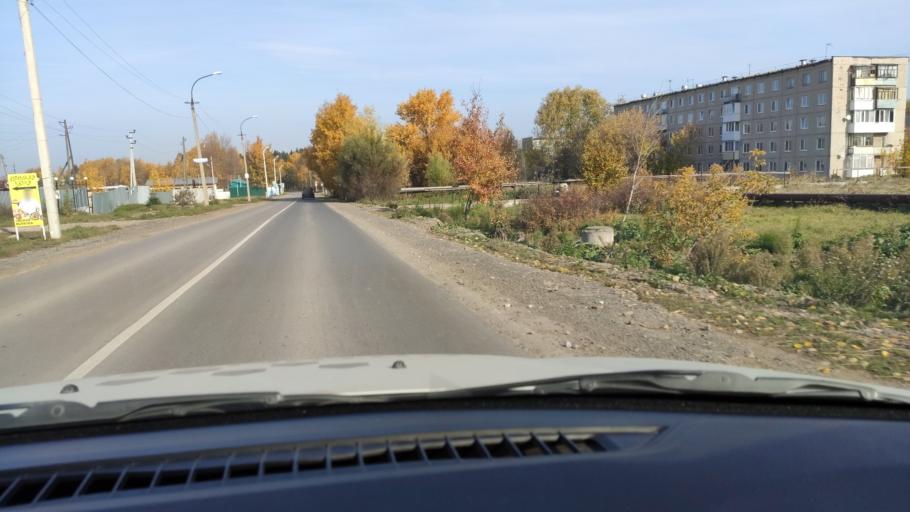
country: RU
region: Perm
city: Sylva
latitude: 58.0286
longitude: 56.7399
